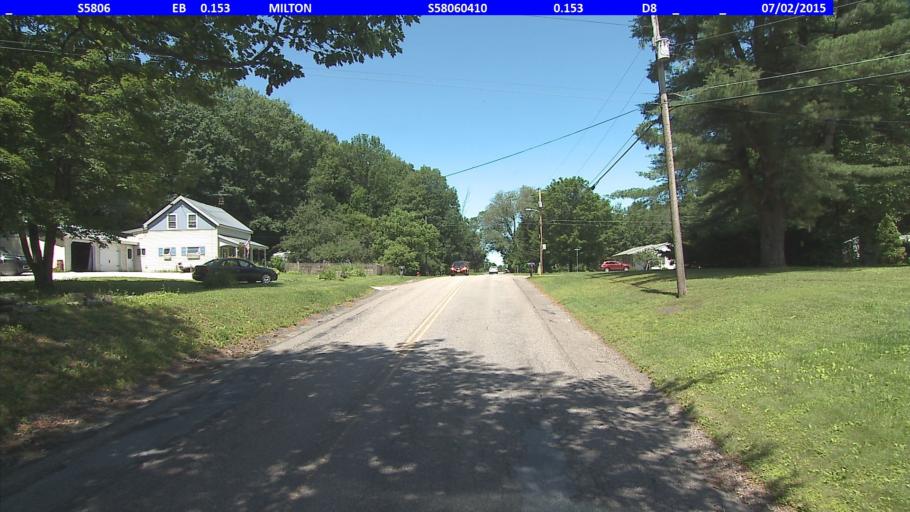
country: US
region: Vermont
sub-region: Chittenden County
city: Milton
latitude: 44.6534
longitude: -73.1167
